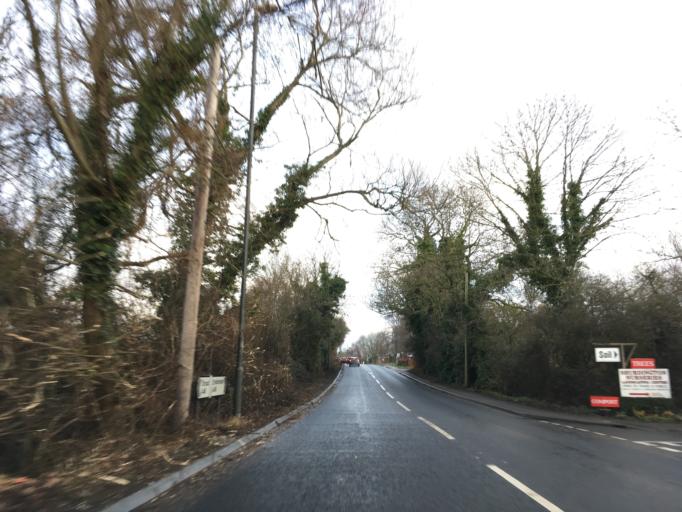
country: GB
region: England
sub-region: Gloucestershire
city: Shurdington
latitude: 51.8571
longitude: -2.1277
